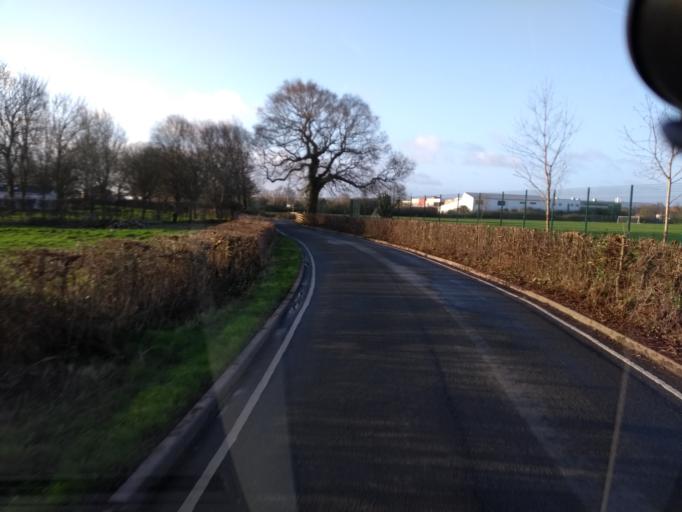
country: GB
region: England
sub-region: Somerset
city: Bridgwater
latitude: 51.1422
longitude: -3.0055
